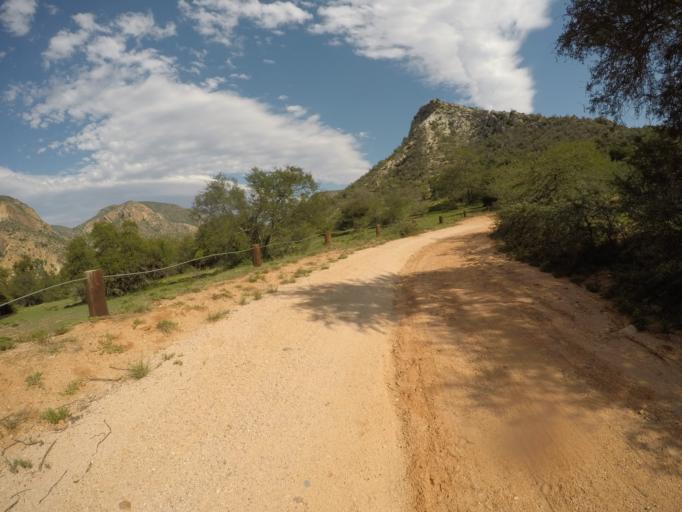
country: ZA
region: Eastern Cape
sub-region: Cacadu District Municipality
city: Kareedouw
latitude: -33.6579
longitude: 24.4317
